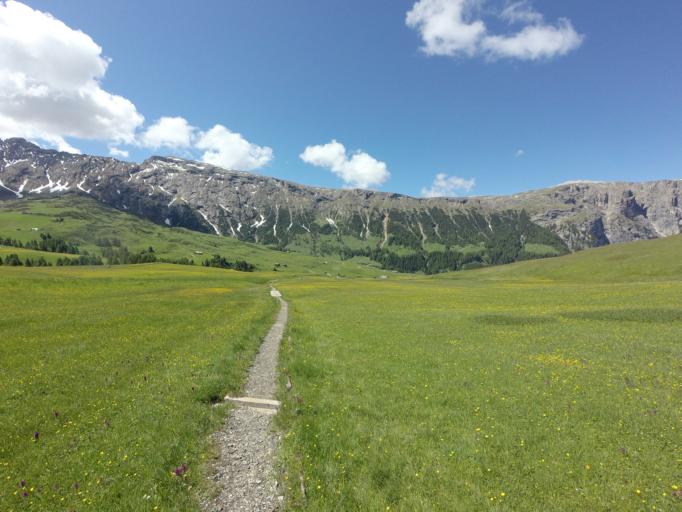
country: IT
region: Trentino-Alto Adige
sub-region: Bolzano
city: Siusi
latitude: 46.5243
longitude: 11.6175
